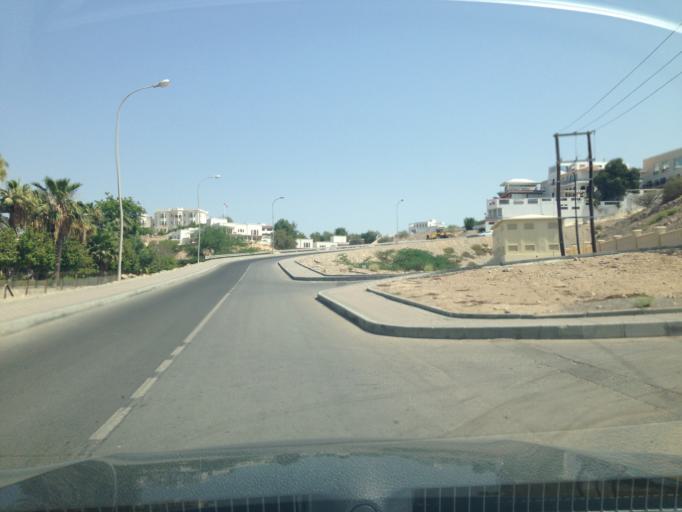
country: OM
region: Muhafazat Masqat
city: Muscat
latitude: 23.6333
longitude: 58.4879
